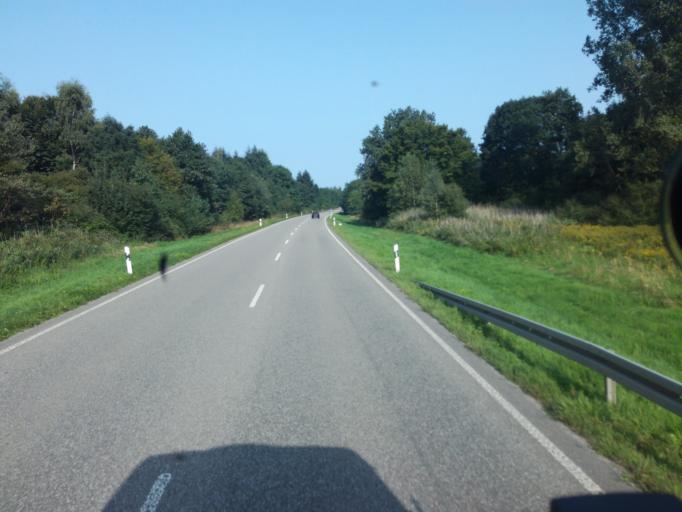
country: DE
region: Baden-Wuerttemberg
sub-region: Karlsruhe Region
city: Rastatt
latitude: 48.8280
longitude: 8.2034
